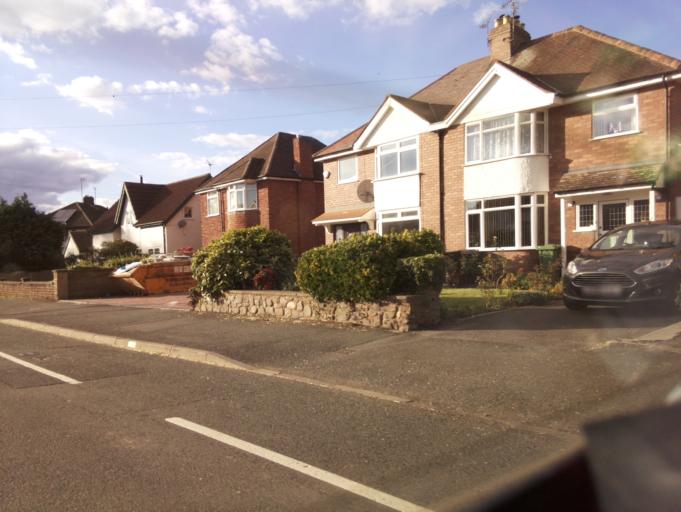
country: GB
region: England
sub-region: Herefordshire
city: Lower Bullingham
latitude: 52.0587
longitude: -2.6855
